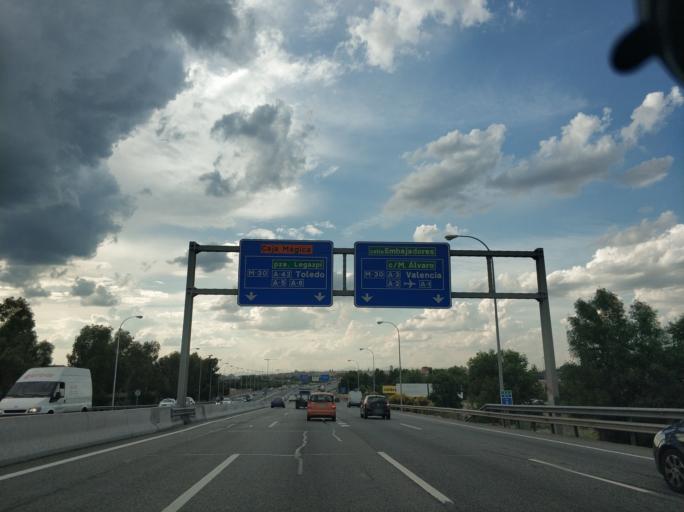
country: ES
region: Madrid
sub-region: Provincia de Madrid
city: Usera
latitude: 40.3751
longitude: -3.6825
